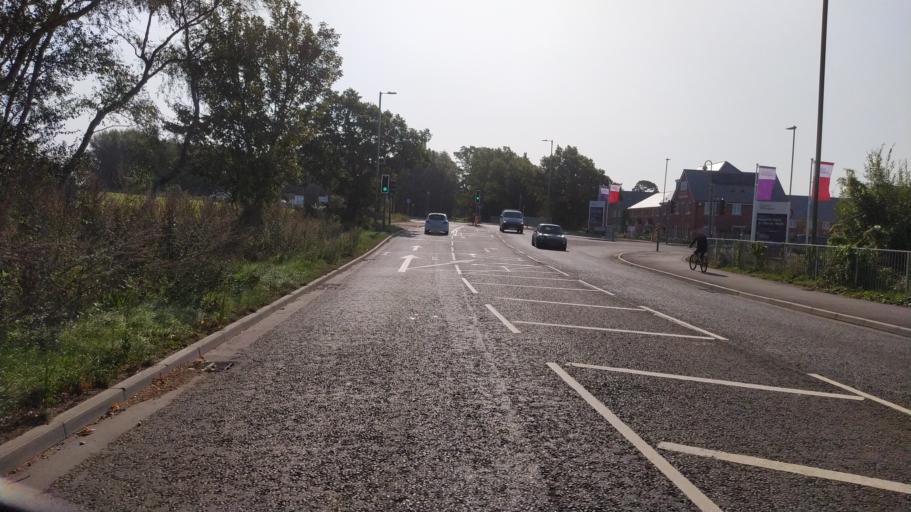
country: GB
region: England
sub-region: Hampshire
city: Bursledon
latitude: 50.8975
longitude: -1.3234
